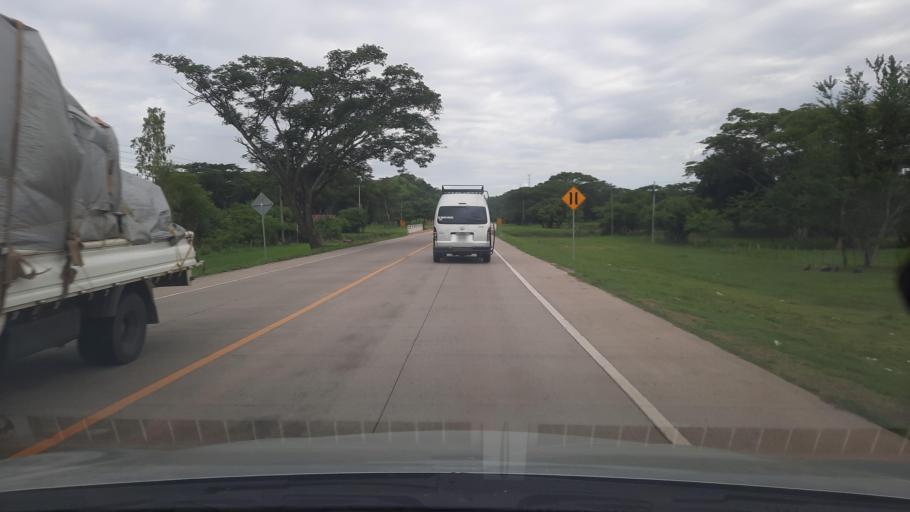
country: NI
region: Chinandega
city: Somotillo
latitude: 12.8728
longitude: -86.8517
